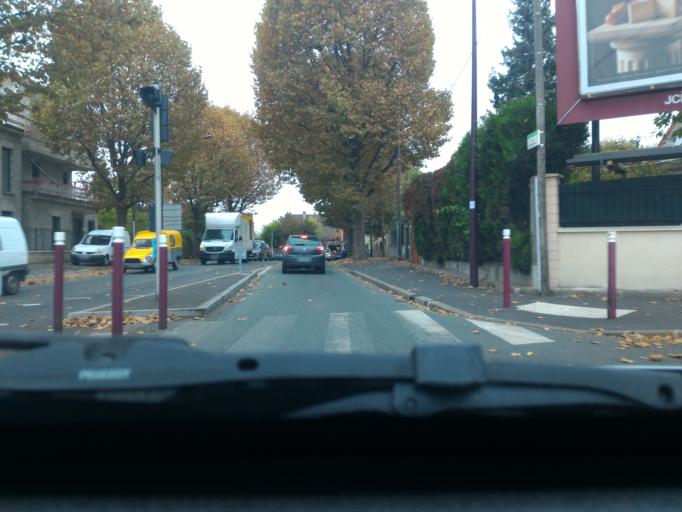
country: FR
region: Ile-de-France
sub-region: Departement du Val-de-Marne
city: L'Hay-les-Roses
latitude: 48.7823
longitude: 2.3412
